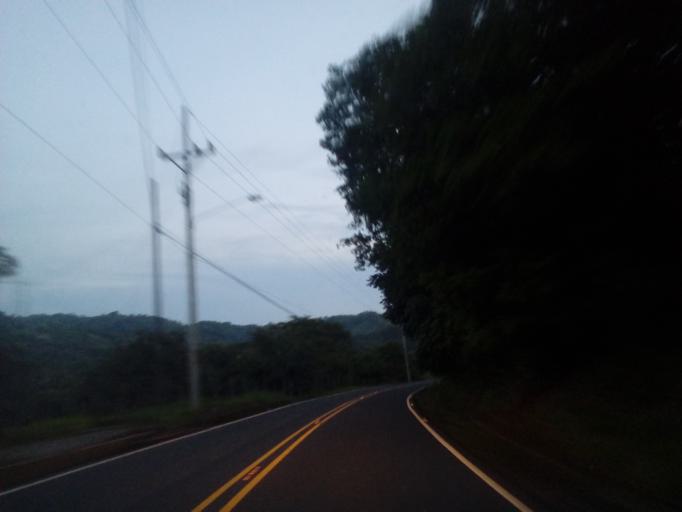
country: CR
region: Guanacaste
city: Samara
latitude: 9.9552
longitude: -85.5165
